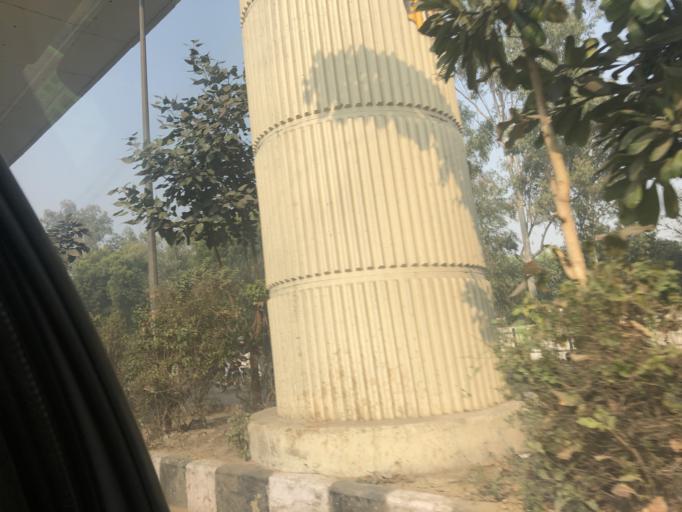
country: IN
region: NCT
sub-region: North West Delhi
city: Pitampura
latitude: 28.6765
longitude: 77.1186
